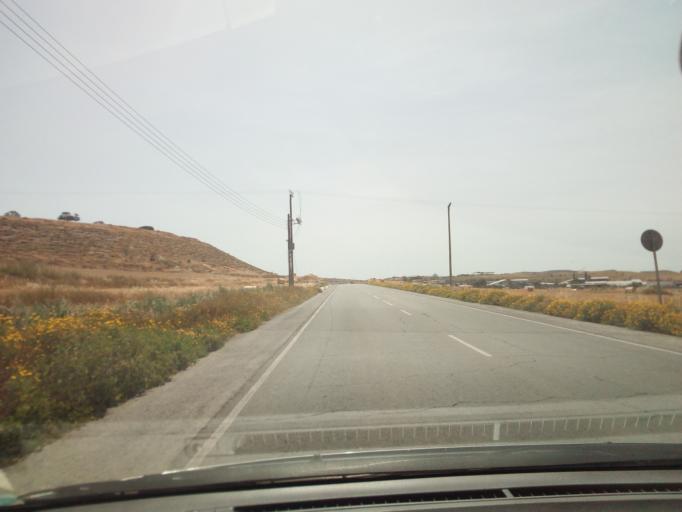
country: CY
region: Larnaka
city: Athienou
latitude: 35.0435
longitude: 33.5497
